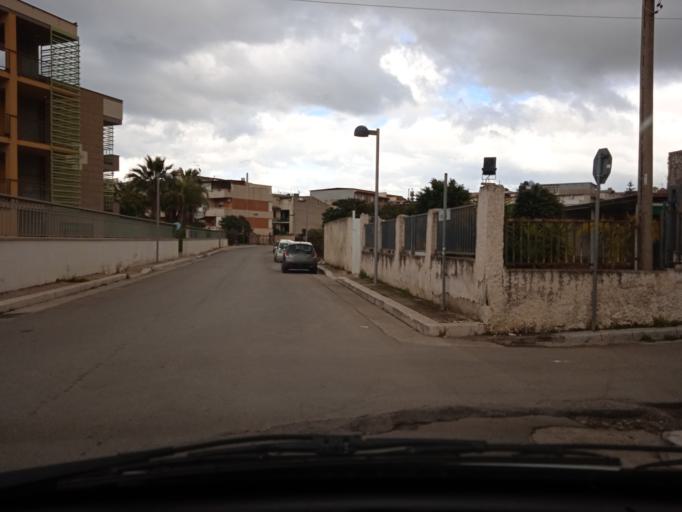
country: IT
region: Sicily
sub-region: Palermo
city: Villabate
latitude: 38.0747
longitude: 13.4420
